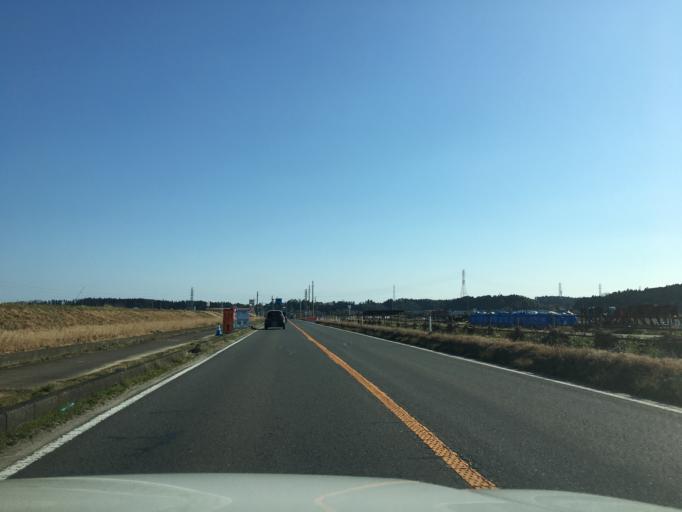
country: JP
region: Ibaraki
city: Mito-shi
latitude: 36.4270
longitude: 140.4214
